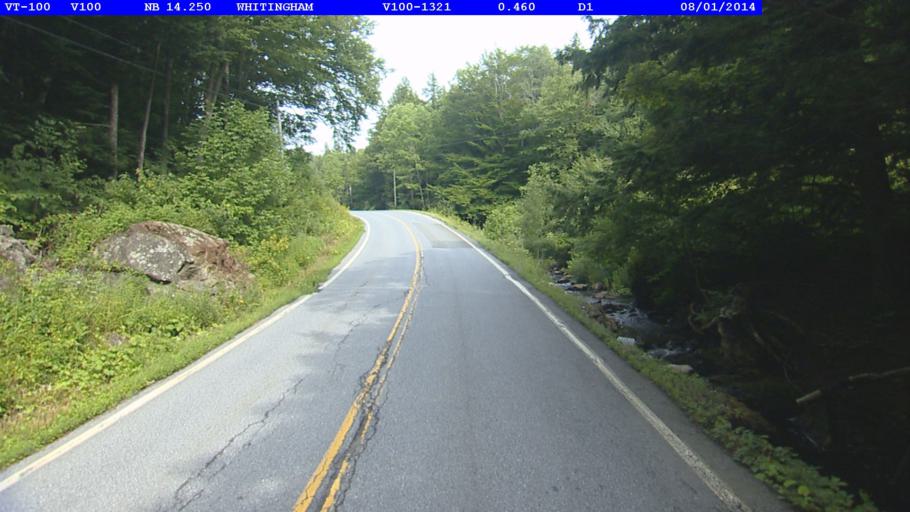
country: US
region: Massachusetts
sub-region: Franklin County
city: Charlemont
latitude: 42.7689
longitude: -72.9209
